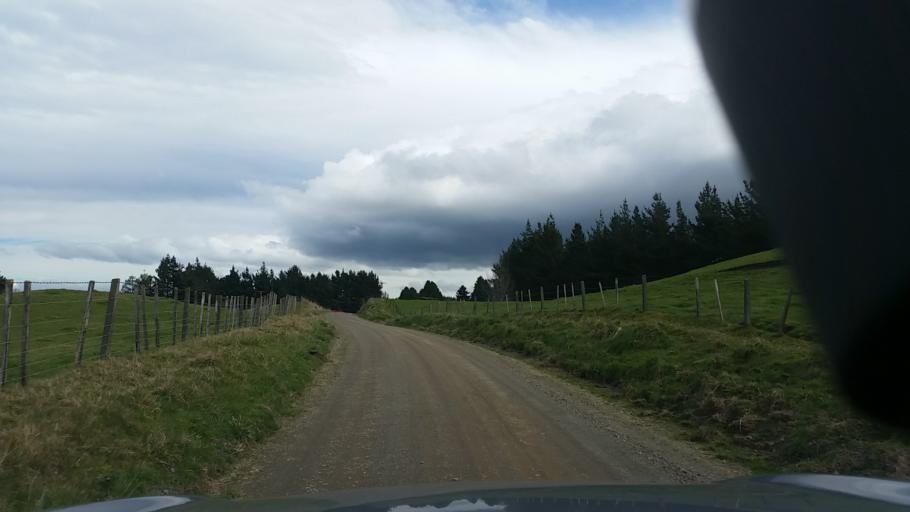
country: NZ
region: Hawke's Bay
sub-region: Napier City
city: Napier
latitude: -39.2051
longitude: 176.9252
